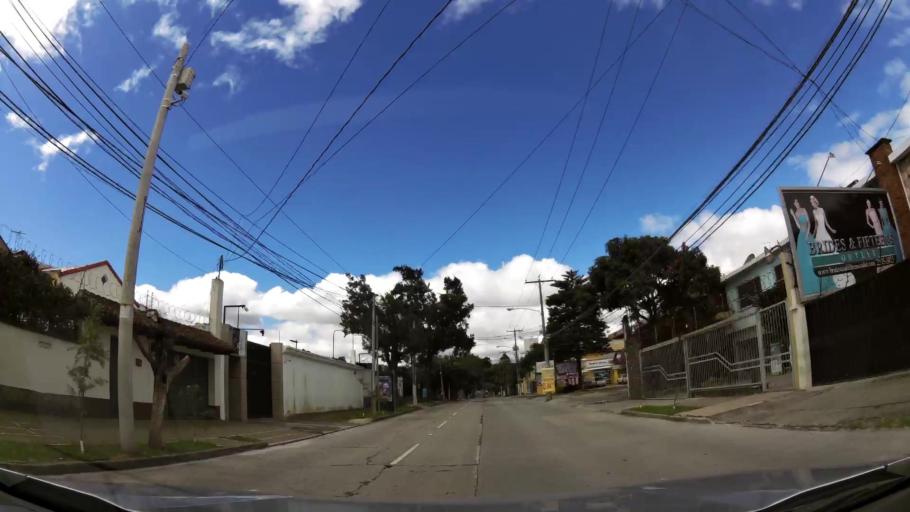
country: GT
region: Guatemala
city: Guatemala City
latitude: 14.6007
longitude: -90.5230
